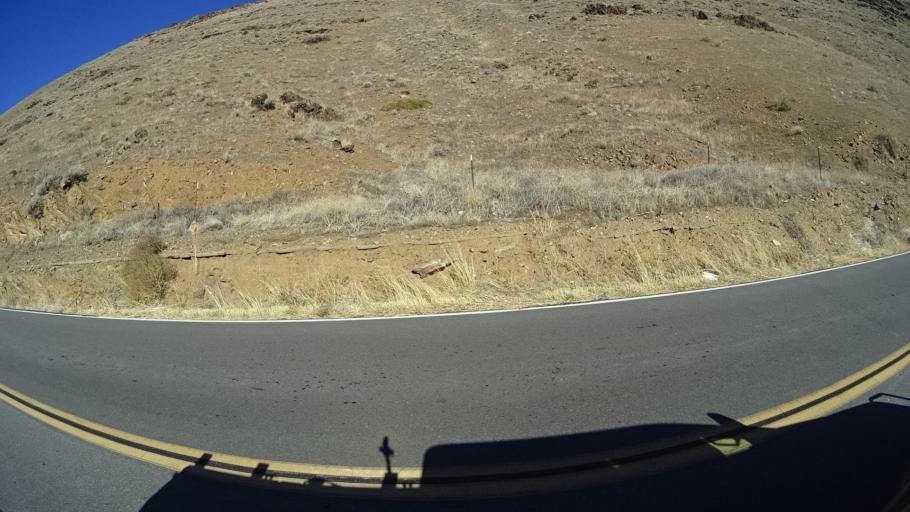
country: US
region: California
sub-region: Kern County
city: Wofford Heights
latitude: 35.6821
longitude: -118.4212
